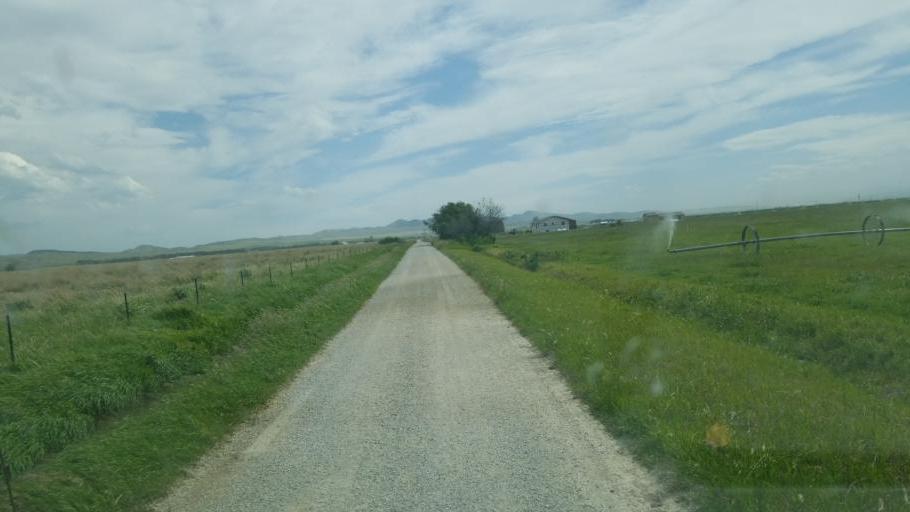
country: US
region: Montana
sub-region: Broadwater County
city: Townsend
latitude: 46.1830
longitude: -111.4719
